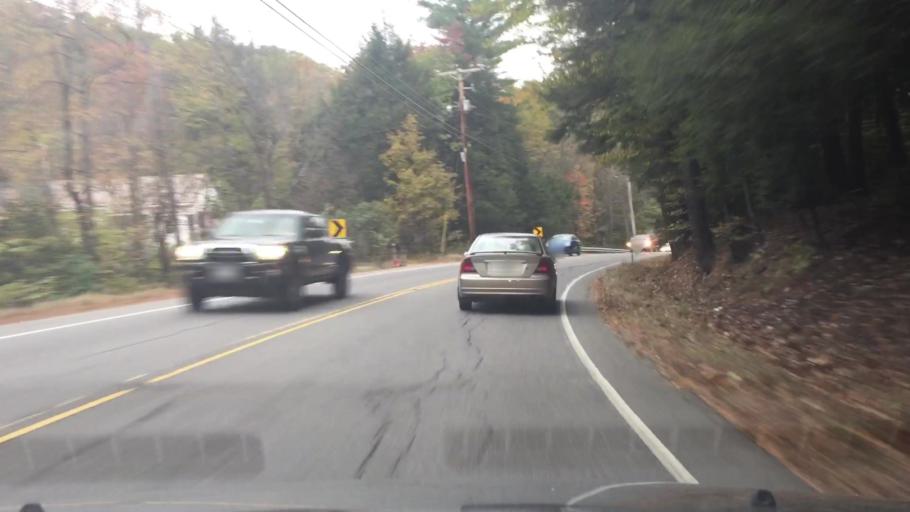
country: US
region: New Hampshire
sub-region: Cheshire County
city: Keene
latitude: 43.0285
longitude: -72.2694
